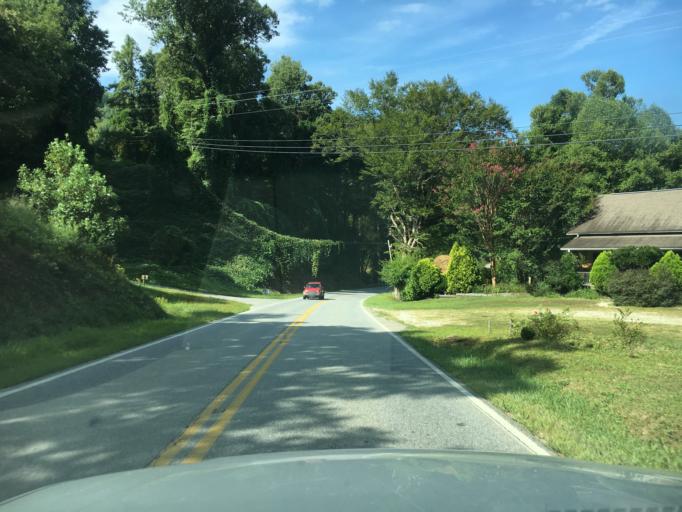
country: US
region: North Carolina
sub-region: Swain County
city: Bryson City
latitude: 35.3376
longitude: -83.5646
